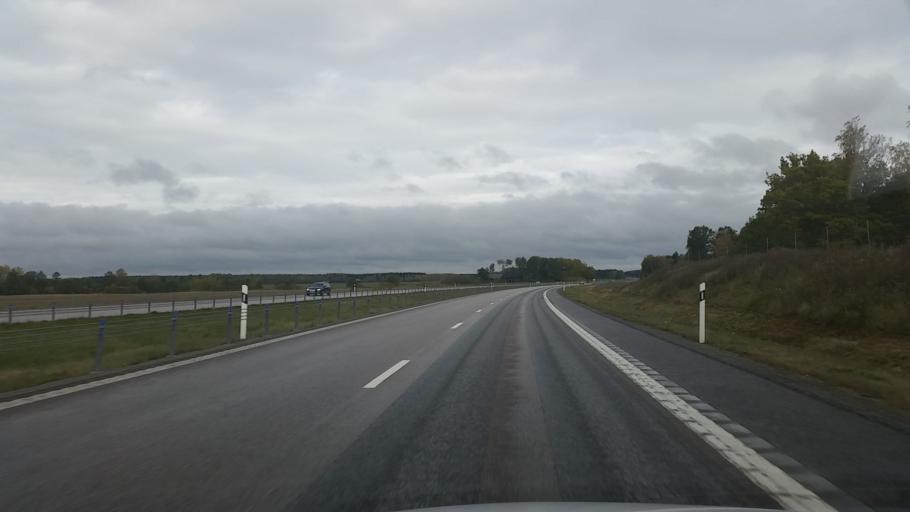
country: SE
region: Uppsala
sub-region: Osthammars Kommun
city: Bjorklinge
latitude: 60.0552
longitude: 17.6165
